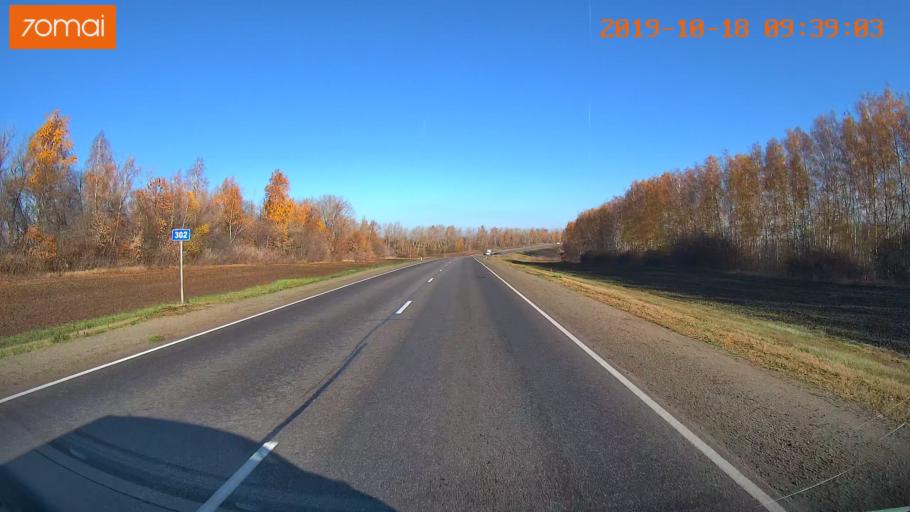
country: RU
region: Tula
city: Yefremov
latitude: 53.2474
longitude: 38.1345
